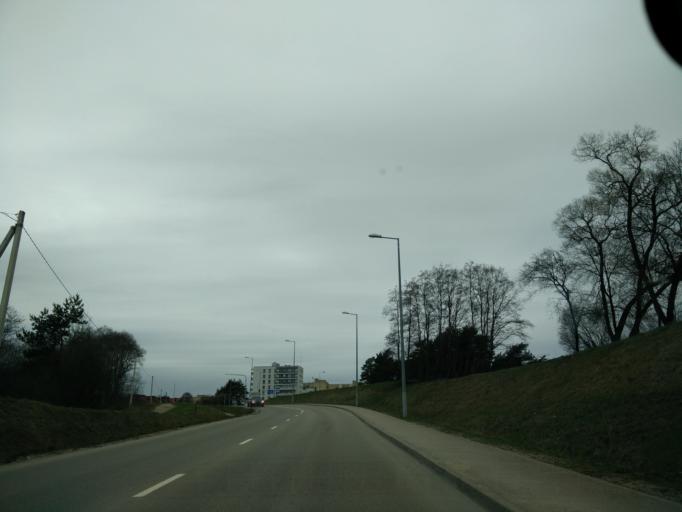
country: LT
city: Grigiskes
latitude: 54.6685
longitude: 25.1074
